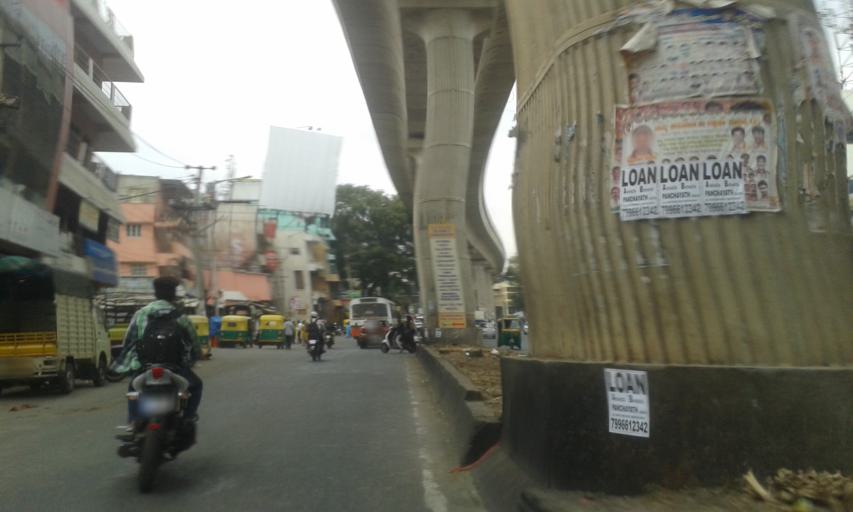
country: IN
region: Karnataka
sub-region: Bangalore Urban
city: Bangalore
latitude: 12.9118
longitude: 77.5729
